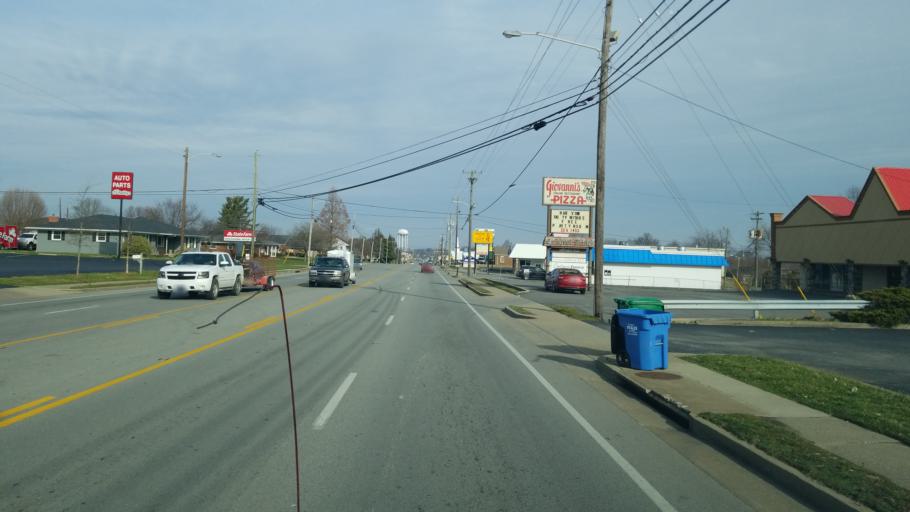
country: US
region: Kentucky
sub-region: Boyle County
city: Danville
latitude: 37.6212
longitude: -84.7745
